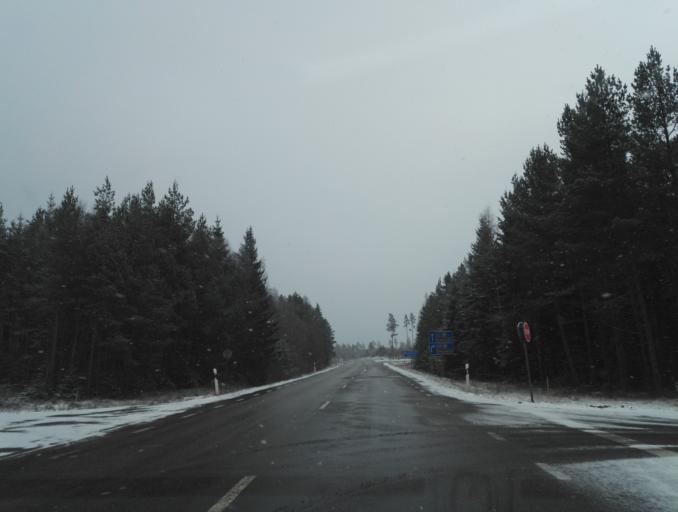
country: SE
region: Kronoberg
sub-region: Uppvidinge Kommun
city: Lenhovda
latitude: 56.9226
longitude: 15.3627
